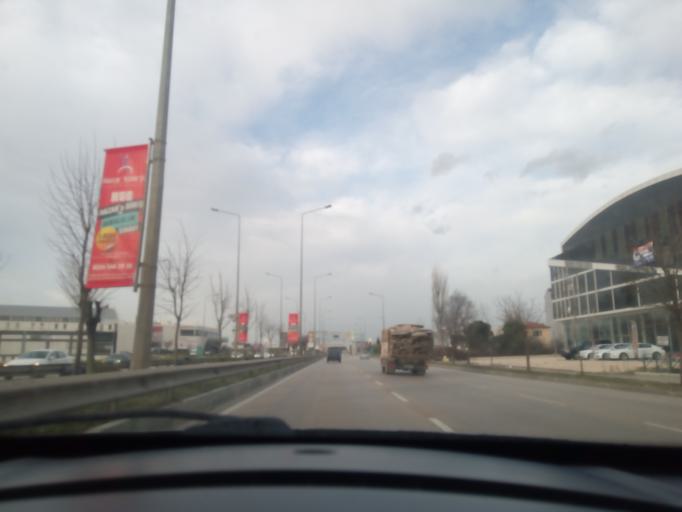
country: TR
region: Bursa
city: Cali
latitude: 40.2132
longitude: 28.9219
